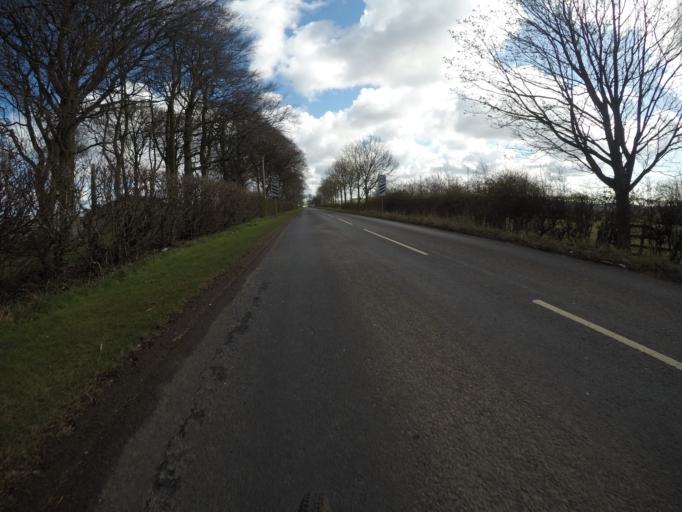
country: GB
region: Scotland
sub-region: North Ayrshire
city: Dreghorn
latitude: 55.5947
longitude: -4.6142
